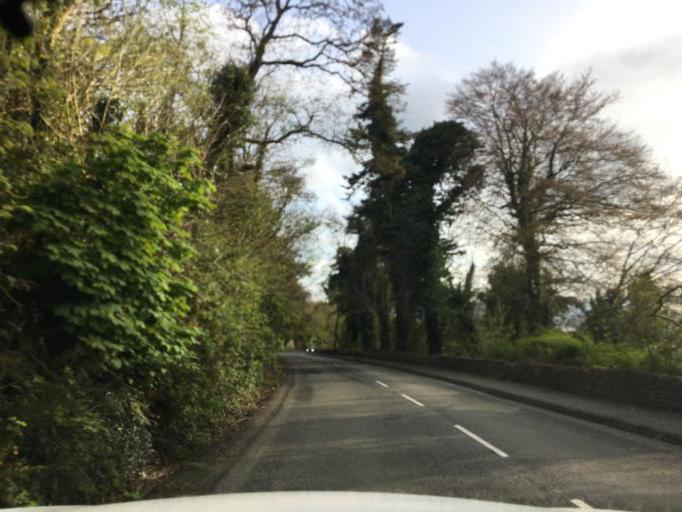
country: IE
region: Leinster
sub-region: Loch Garman
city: New Ross
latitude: 52.4032
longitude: -6.9387
